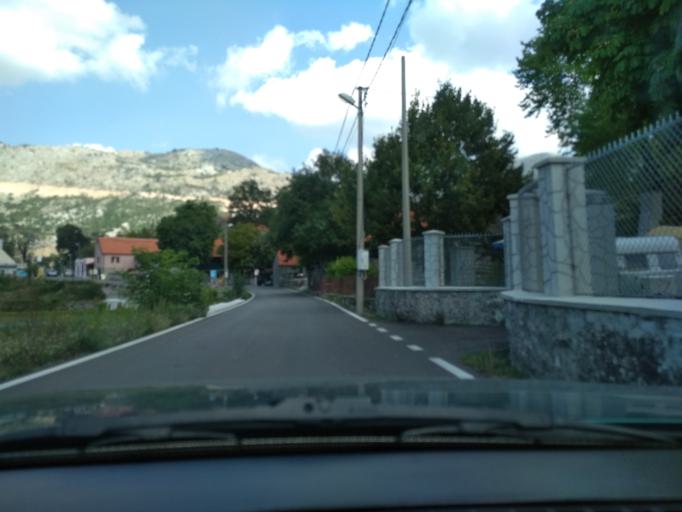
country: ME
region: Kotor
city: Kotor
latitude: 42.4315
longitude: 18.8283
